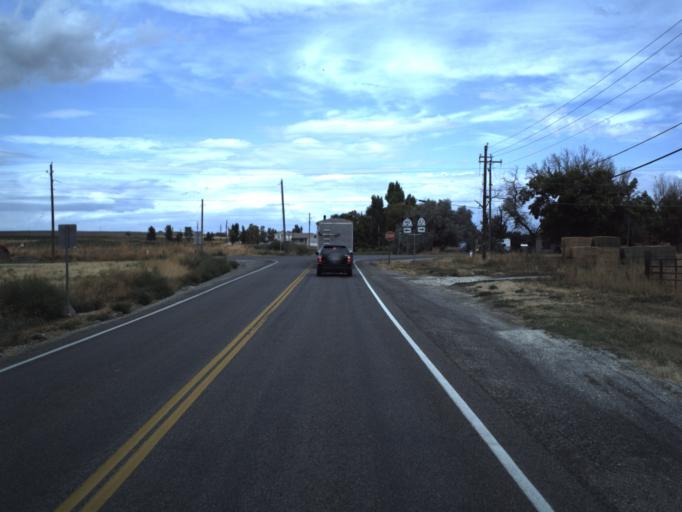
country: US
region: Utah
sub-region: Cache County
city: Benson
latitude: 41.8617
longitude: -111.9998
